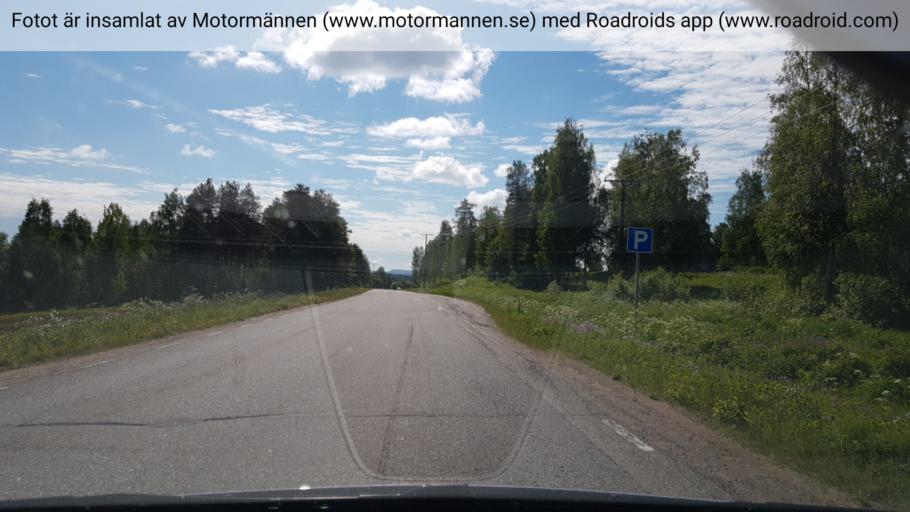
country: FI
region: Lapland
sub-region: Torniolaakso
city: Pello
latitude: 66.6561
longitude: 23.8560
